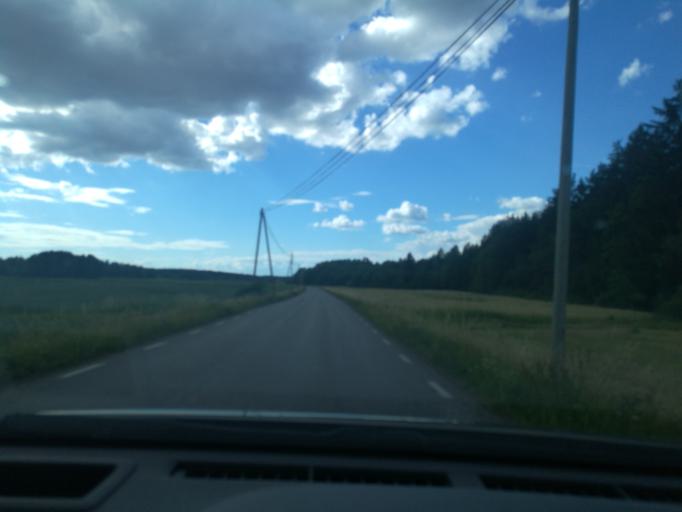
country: SE
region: Soedermanland
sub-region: Eskilstuna Kommun
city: Arla
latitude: 59.4480
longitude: 16.7479
